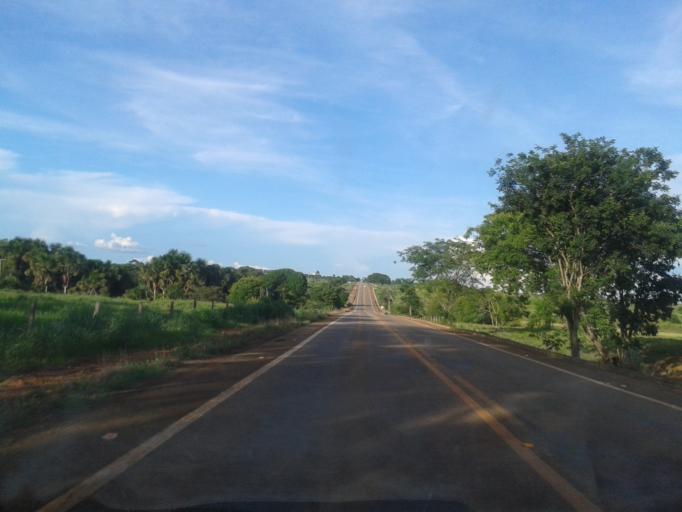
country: BR
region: Goias
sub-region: Sao Miguel Do Araguaia
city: Sao Miguel do Araguaia
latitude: -13.4402
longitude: -50.2883
